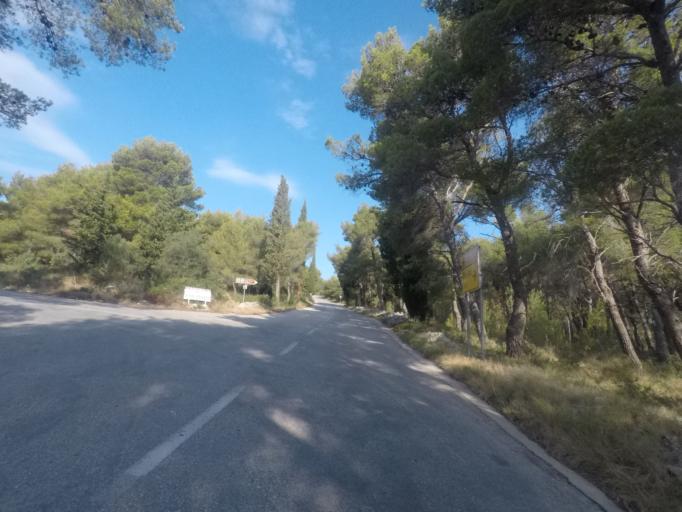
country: HR
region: Splitsko-Dalmatinska
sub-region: Grad Hvar
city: Hvar
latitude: 43.1761
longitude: 16.4389
